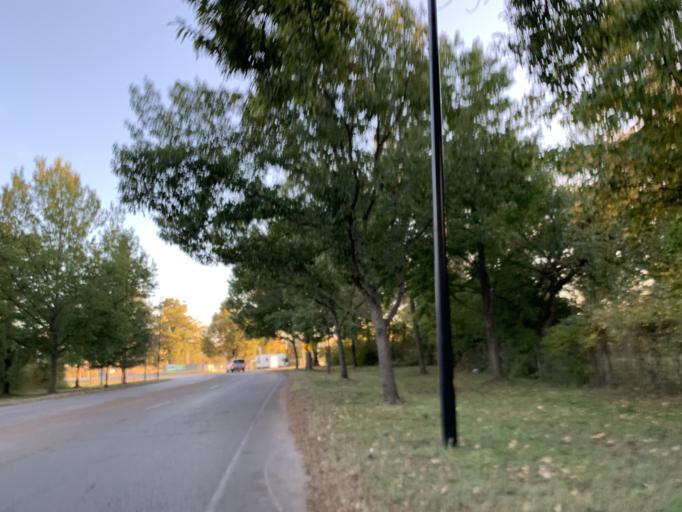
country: US
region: Kentucky
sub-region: Jefferson County
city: Shively
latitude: 38.2338
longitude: -85.8308
